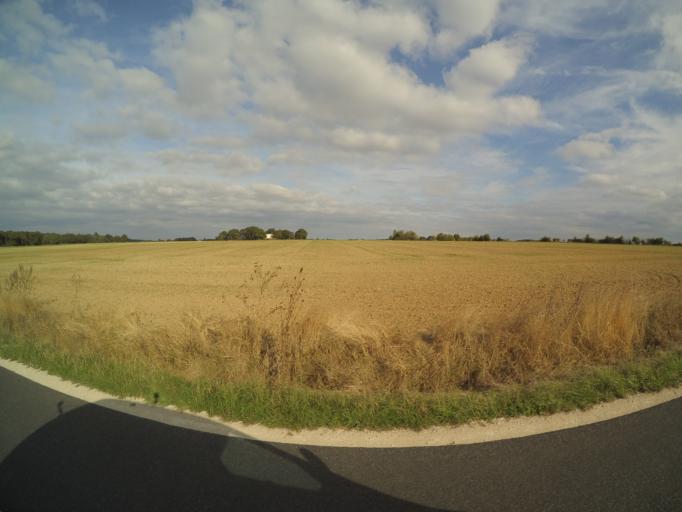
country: FR
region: Centre
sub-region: Departement d'Indre-et-Loire
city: Nazelles-Negron
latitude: 47.4496
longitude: 0.9560
